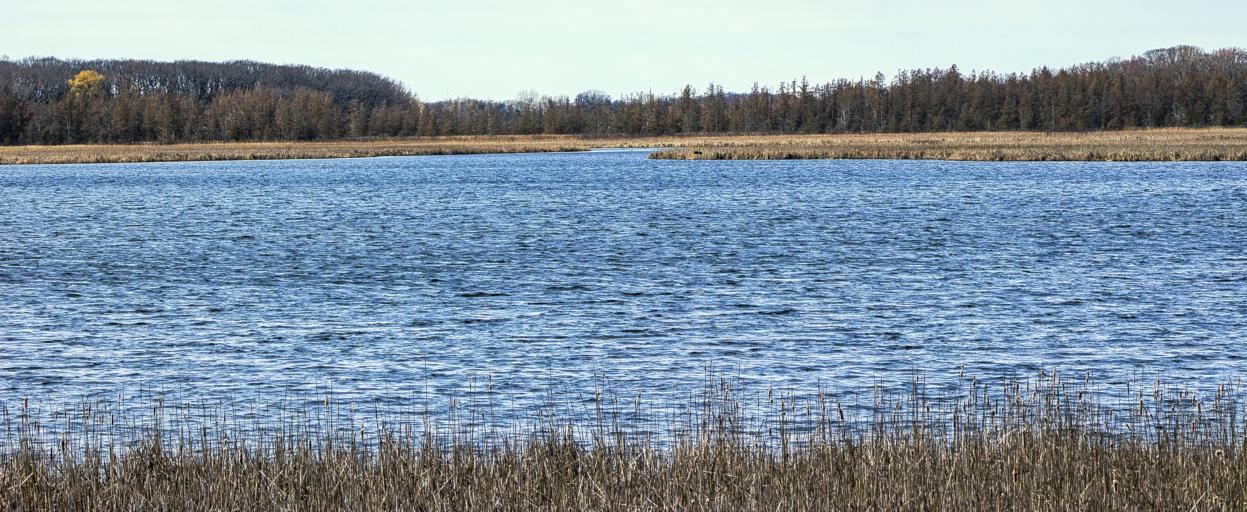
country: US
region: Wisconsin
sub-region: Jefferson County
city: Lake Mills
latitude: 43.0652
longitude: -88.9258
